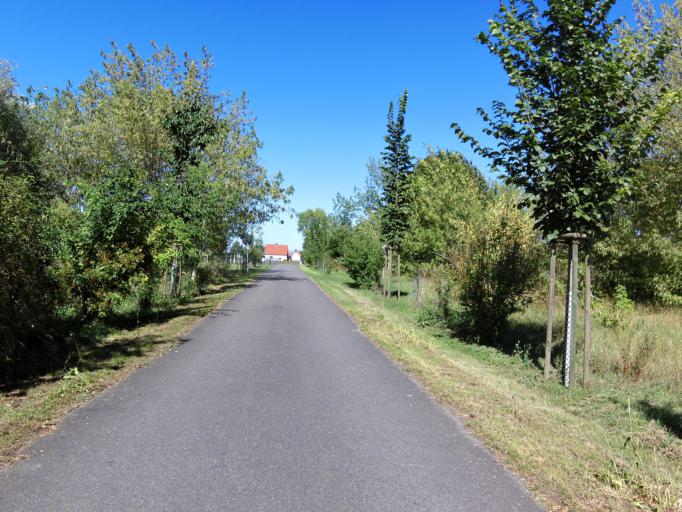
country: DE
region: Saxony-Anhalt
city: Elster
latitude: 51.8305
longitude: 12.8010
